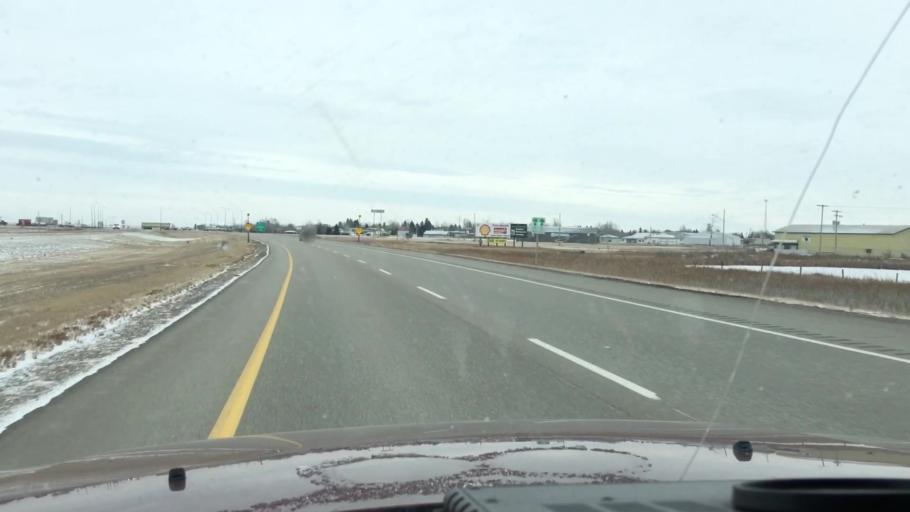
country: CA
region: Saskatchewan
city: Watrous
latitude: 51.2723
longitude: -106.0018
